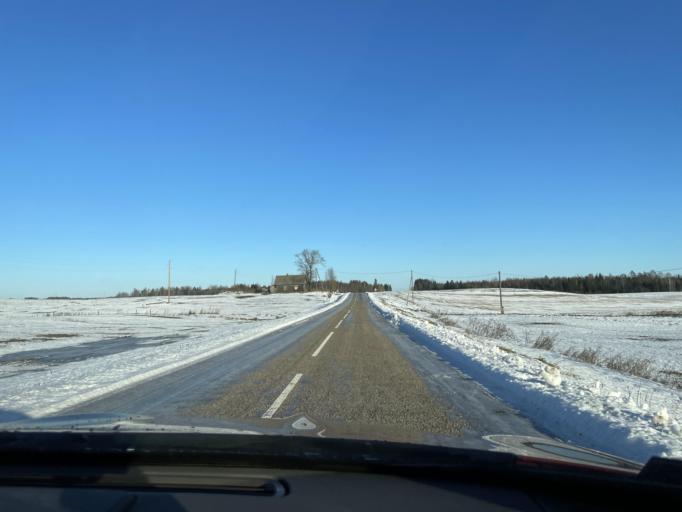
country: LV
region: Ludzas Rajons
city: Ludza
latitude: 56.4434
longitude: 27.5416
